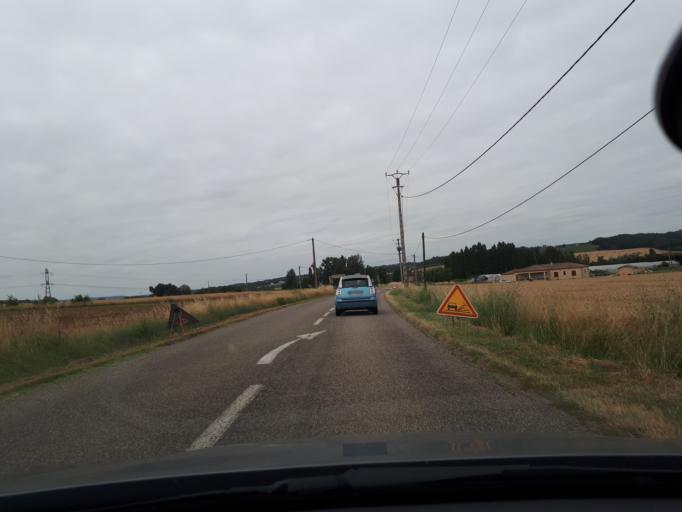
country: FR
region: Midi-Pyrenees
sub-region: Departement du Tarn-et-Garonne
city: Auvillar
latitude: 44.0464
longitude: 0.8596
